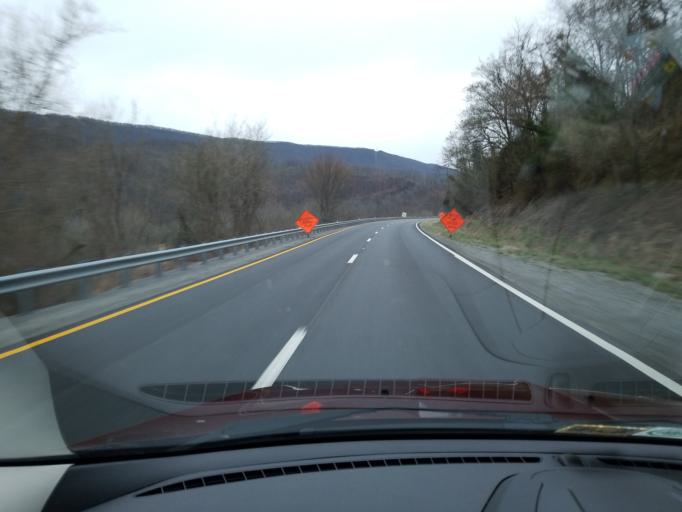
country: US
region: Virginia
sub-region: Giles County
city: Narrows
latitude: 37.3767
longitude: -80.8493
